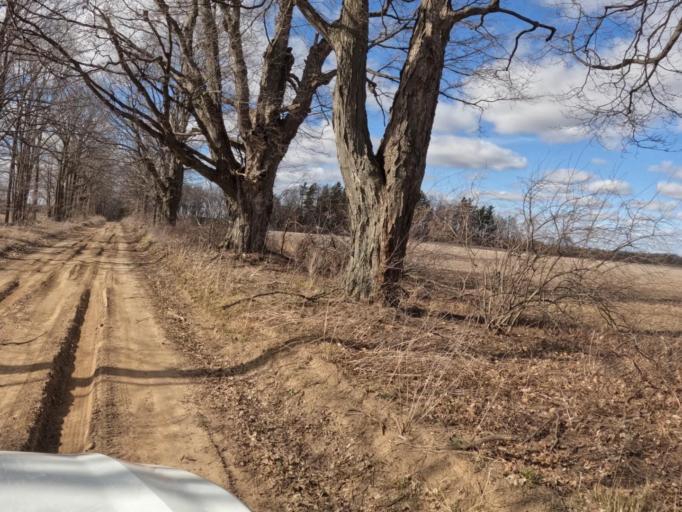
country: CA
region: Ontario
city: Norfolk County
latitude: 42.7559
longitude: -80.3125
